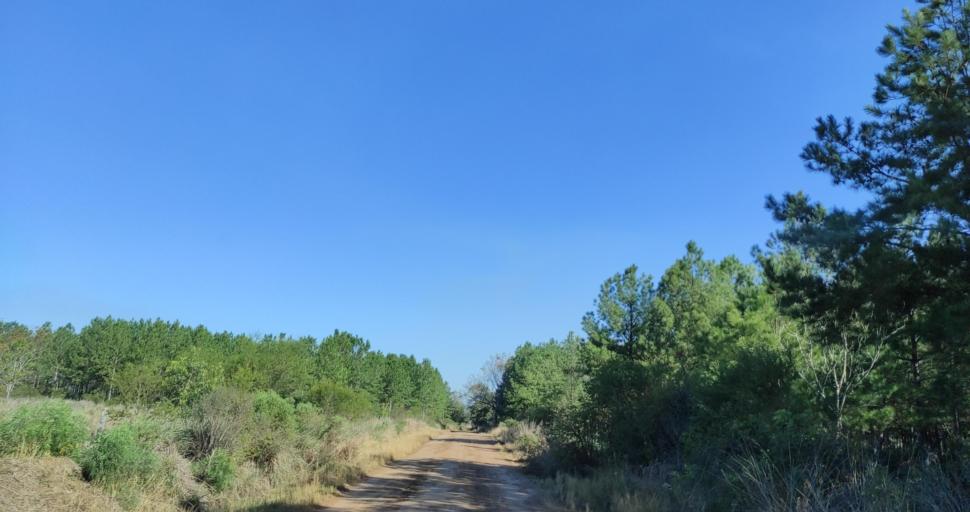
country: AR
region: Misiones
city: Cerro Cora
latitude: -27.6509
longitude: -55.6578
